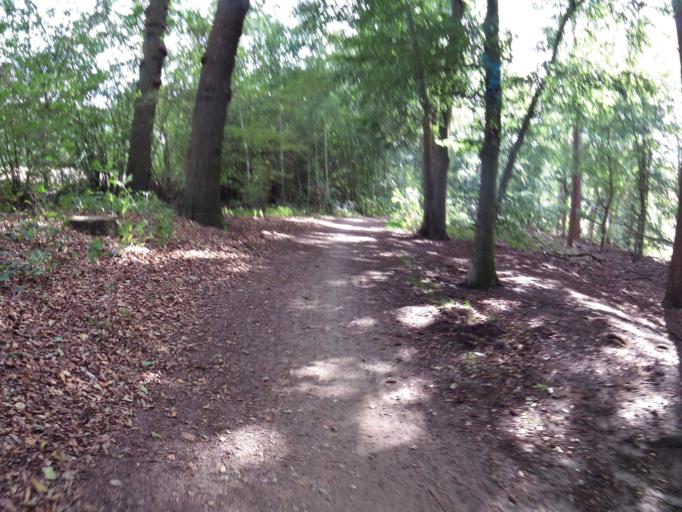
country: NL
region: Gelderland
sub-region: Gemeente Aalten
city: Bredevoort
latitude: 51.9357
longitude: 6.6061
